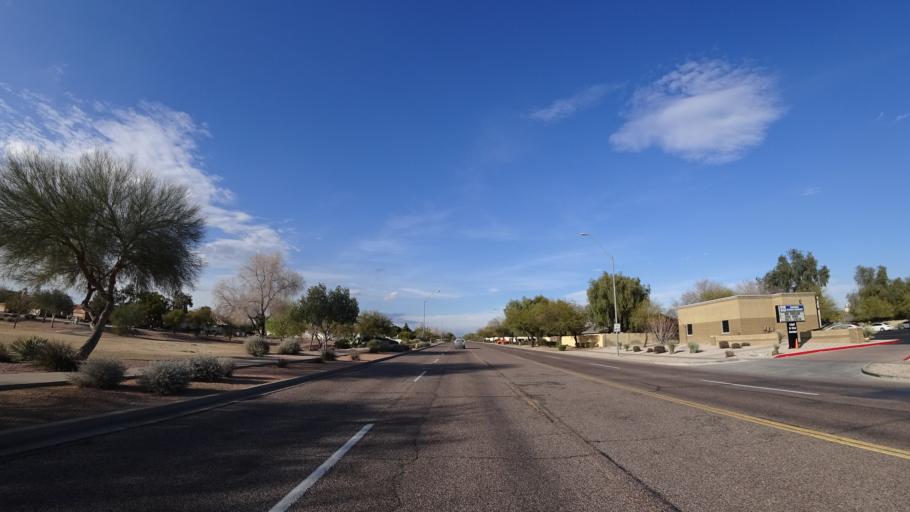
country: US
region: Arizona
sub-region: Maricopa County
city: Sun City
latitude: 33.6441
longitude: -112.2550
